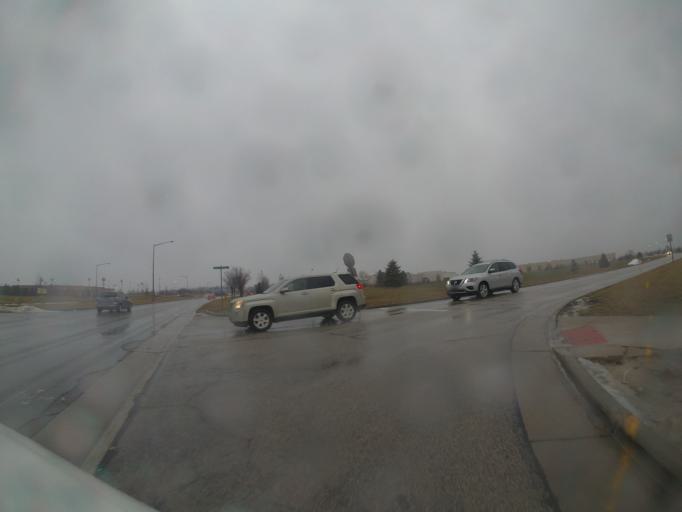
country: US
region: Ohio
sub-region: Wood County
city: Perrysburg
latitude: 41.5474
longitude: -83.5839
